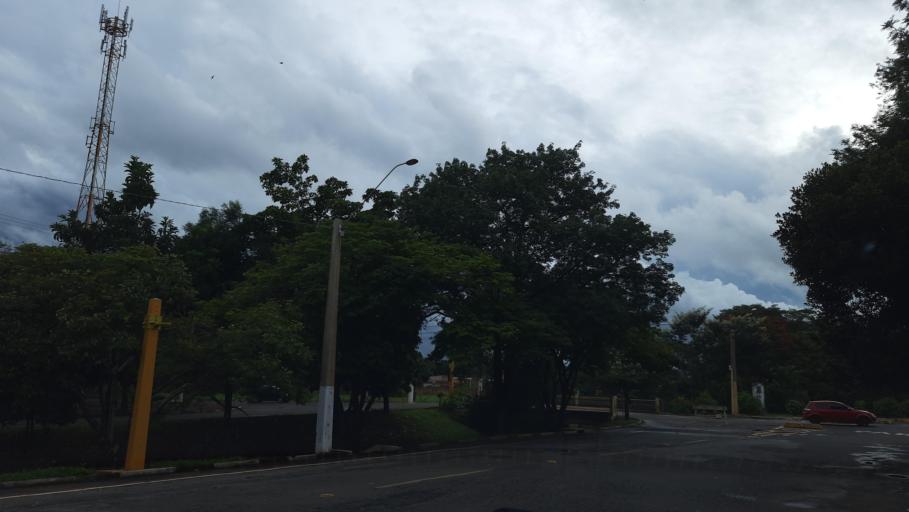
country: BR
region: Sao Paulo
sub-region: Casa Branca
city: Casa Branca
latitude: -21.7674
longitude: -47.0912
